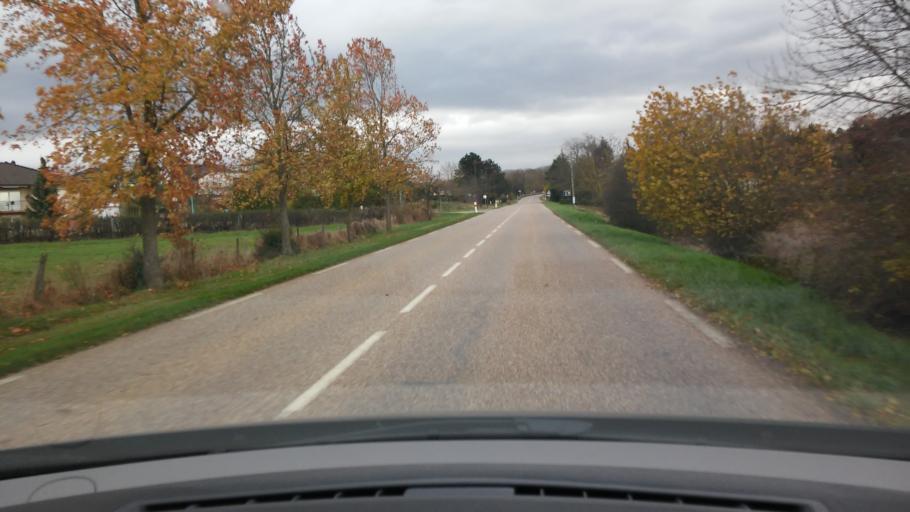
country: FR
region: Lorraine
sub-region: Departement de la Moselle
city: Saint-Julien-les-Metz
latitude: 49.1551
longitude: 6.2425
